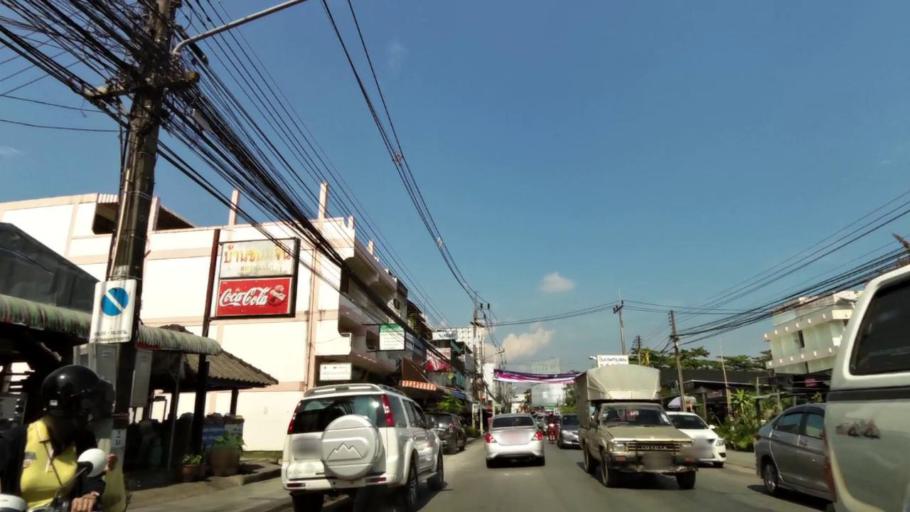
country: TH
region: Chiang Rai
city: Chiang Rai
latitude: 19.9054
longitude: 99.8285
